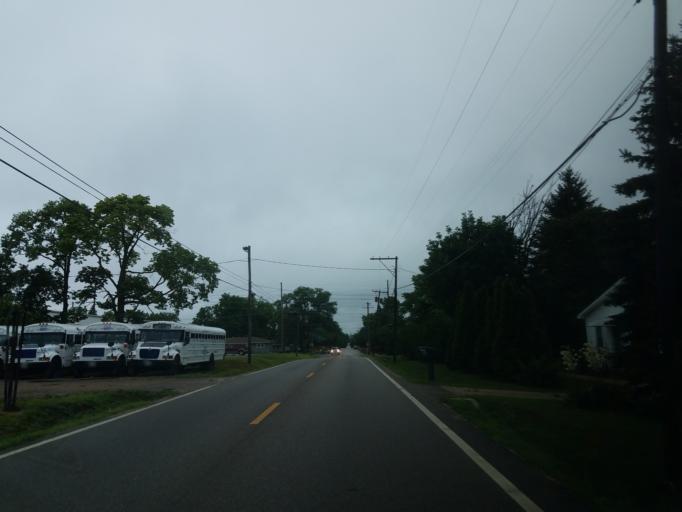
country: US
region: Illinois
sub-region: McLean County
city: Bloomington
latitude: 40.4624
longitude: -88.9816
